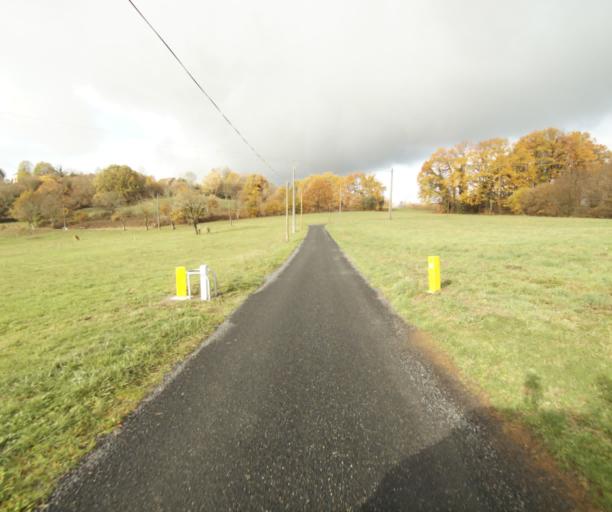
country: FR
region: Limousin
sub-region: Departement de la Correze
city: Sainte-Fereole
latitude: 45.2258
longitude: 1.6317
